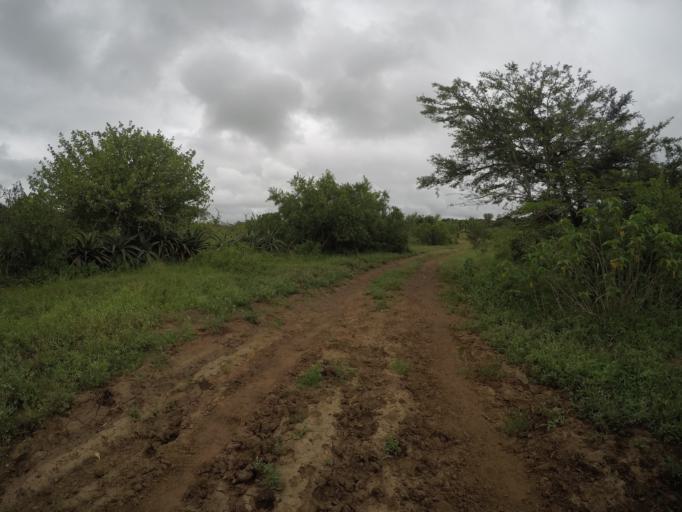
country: ZA
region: KwaZulu-Natal
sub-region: uThungulu District Municipality
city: Empangeni
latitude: -28.6057
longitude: 31.8529
